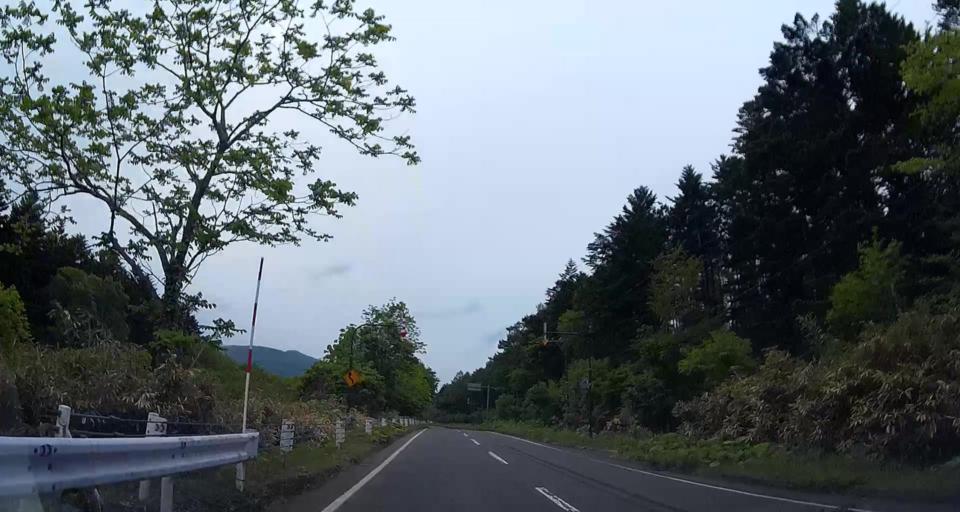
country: JP
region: Hokkaido
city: Shiraoi
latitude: 42.6369
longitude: 141.2370
